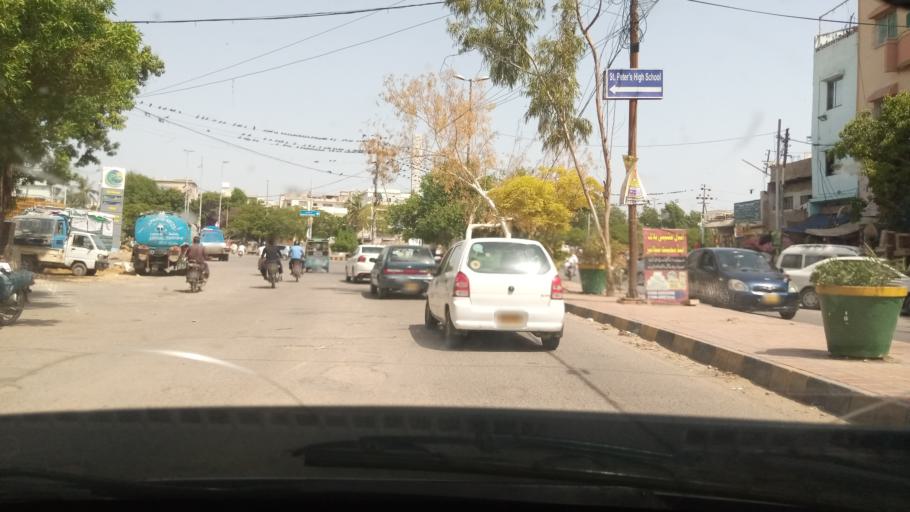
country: PK
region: Sindh
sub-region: Karachi District
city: Karachi
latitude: 24.8733
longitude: 67.0480
